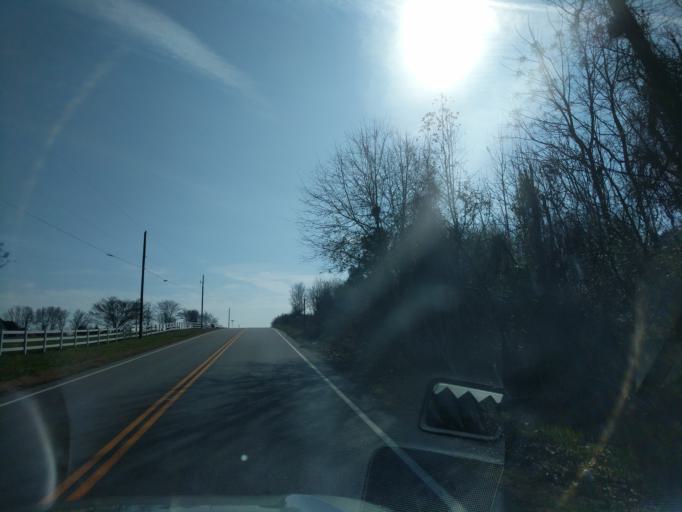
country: US
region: South Carolina
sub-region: Spartanburg County
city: Wellford
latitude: 34.8769
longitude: -82.1008
